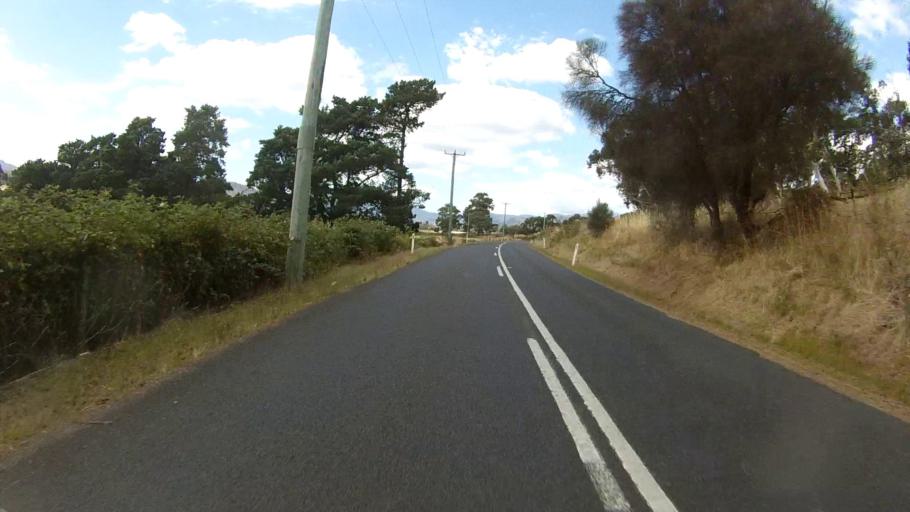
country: AU
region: Tasmania
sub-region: Derwent Valley
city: New Norfolk
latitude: -42.7599
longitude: 146.9932
